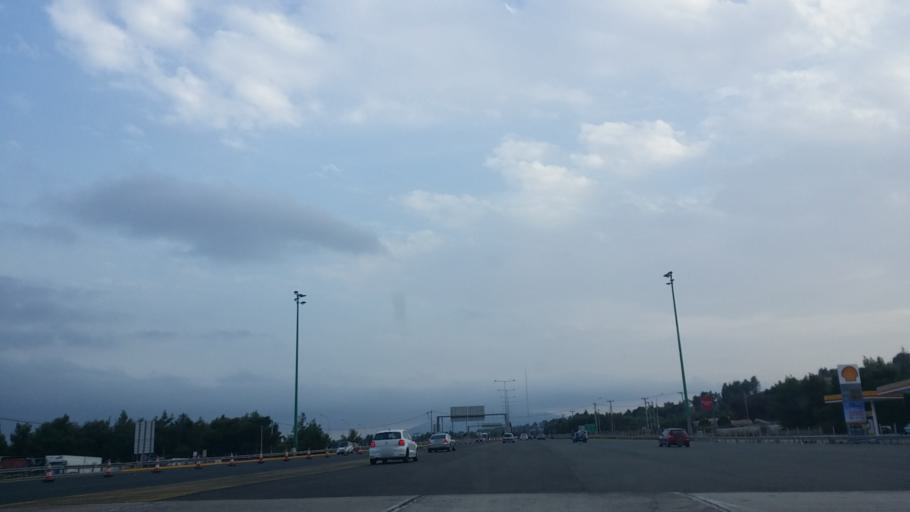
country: GR
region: Attica
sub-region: Nomarchia Anatolikis Attikis
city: Agios Stefanos
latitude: 38.1753
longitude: 23.8543
